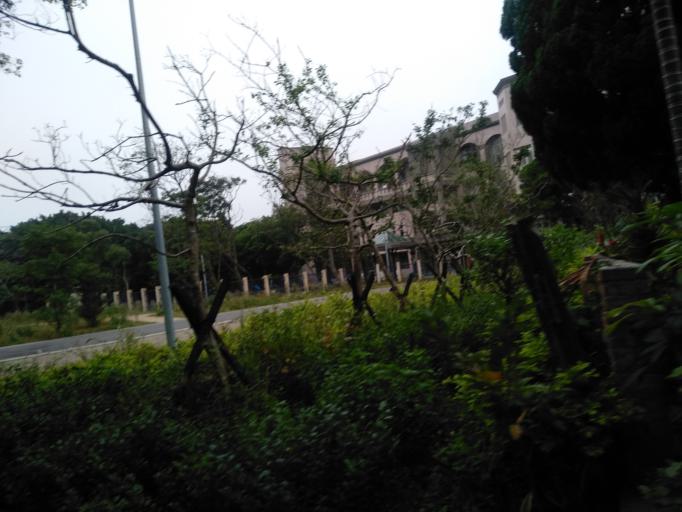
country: TW
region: Taiwan
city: Taoyuan City
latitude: 24.9988
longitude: 121.1622
